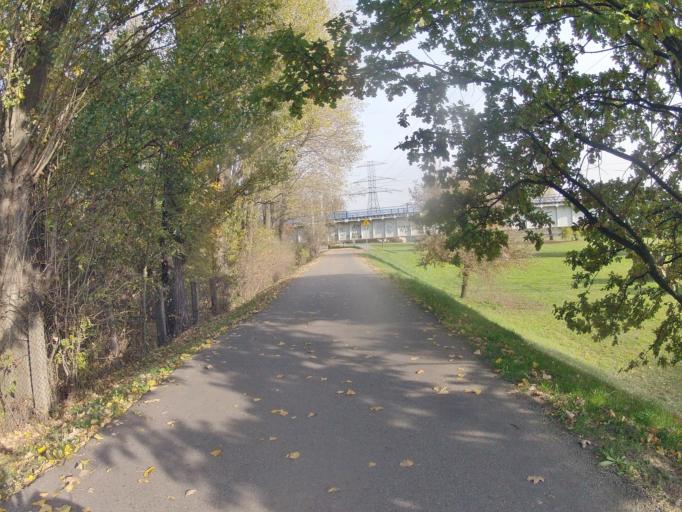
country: PL
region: Lesser Poland Voivodeship
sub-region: Krakow
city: Krakow
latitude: 50.0537
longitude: 19.9693
